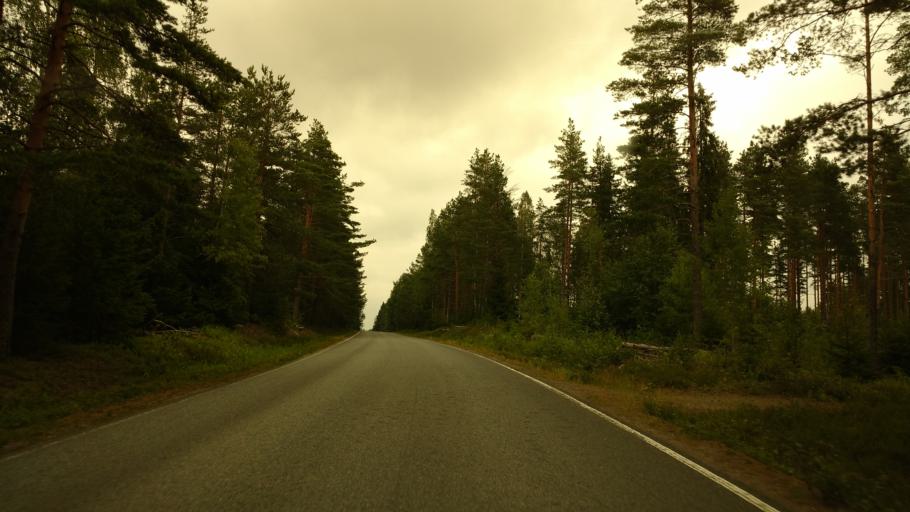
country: FI
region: Haeme
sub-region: Forssa
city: Ypaejae
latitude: 60.7491
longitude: 23.2042
